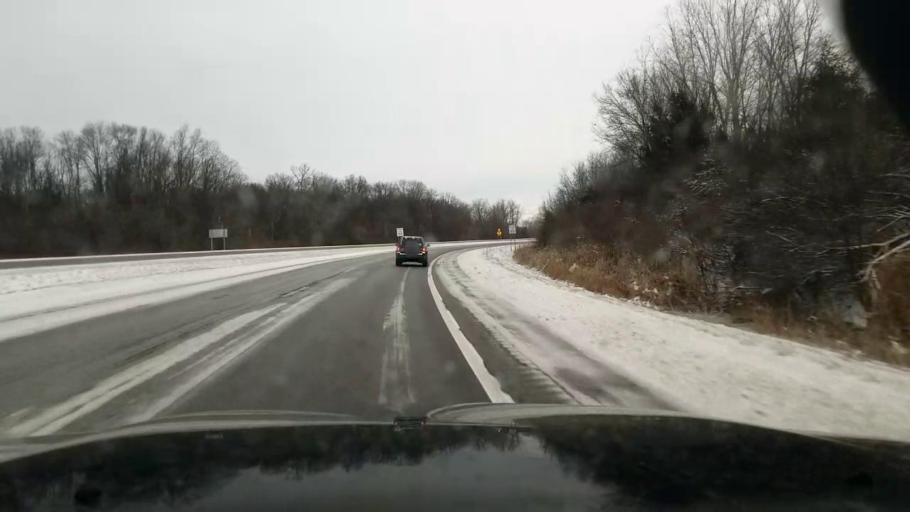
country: US
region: Michigan
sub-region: Jackson County
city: Jackson
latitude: 42.2306
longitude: -84.4752
